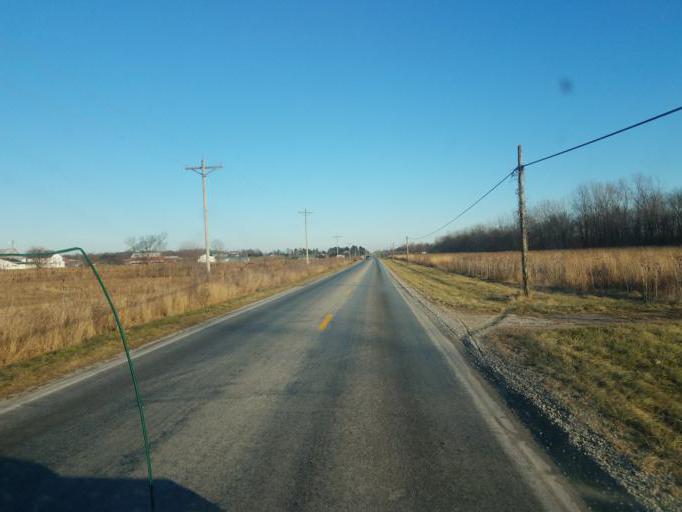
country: US
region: Ohio
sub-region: Hardin County
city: Kenton
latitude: 40.6242
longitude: -83.5266
